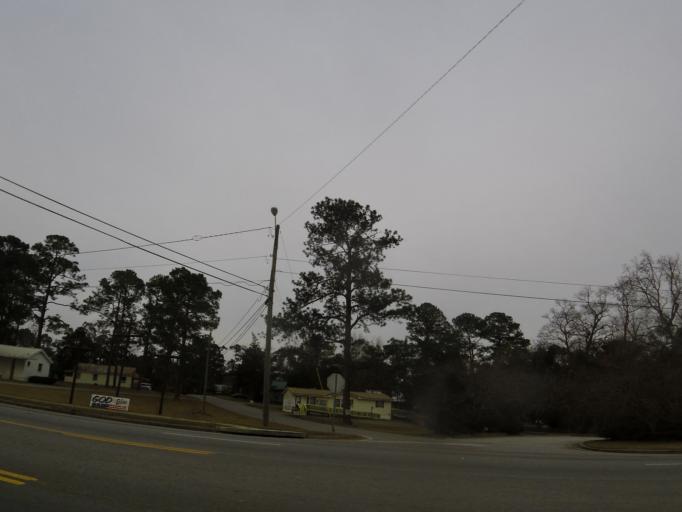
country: US
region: Georgia
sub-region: Grady County
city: Cairo
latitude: 30.8821
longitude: -84.1997
